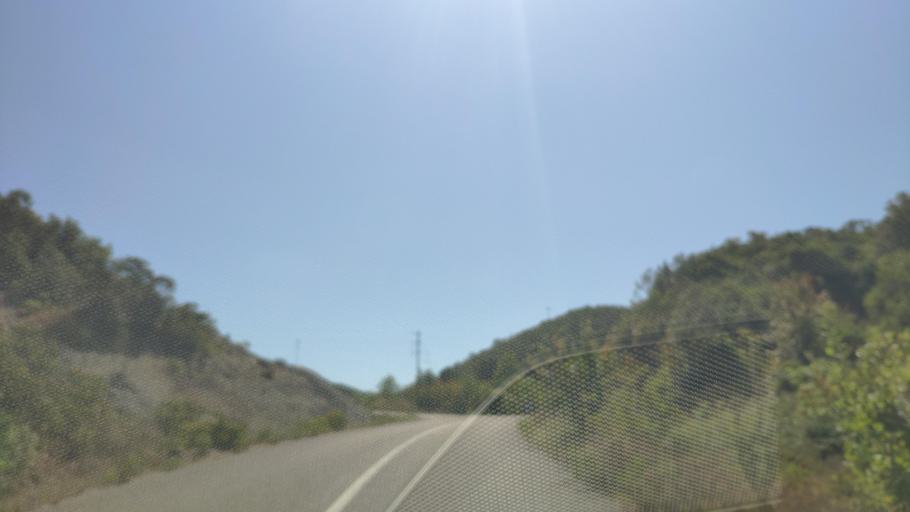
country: GR
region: Central Greece
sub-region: Nomos Evrytanias
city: Kerasochori
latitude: 39.0053
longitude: 21.5360
